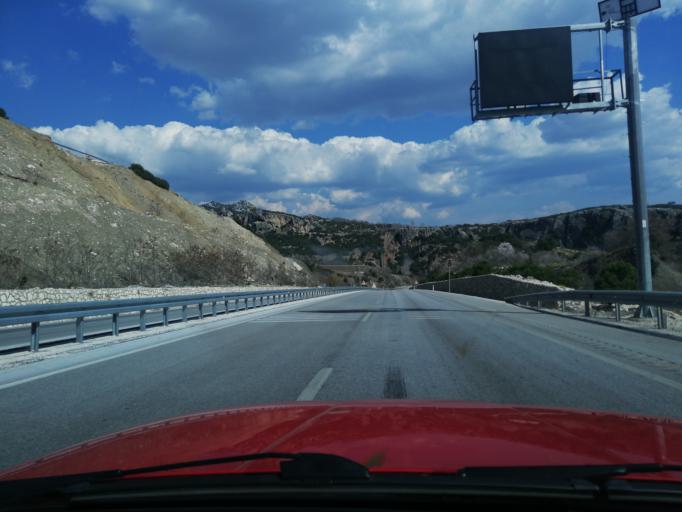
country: TR
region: Burdur
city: Celtikci
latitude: 37.5849
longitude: 30.4339
